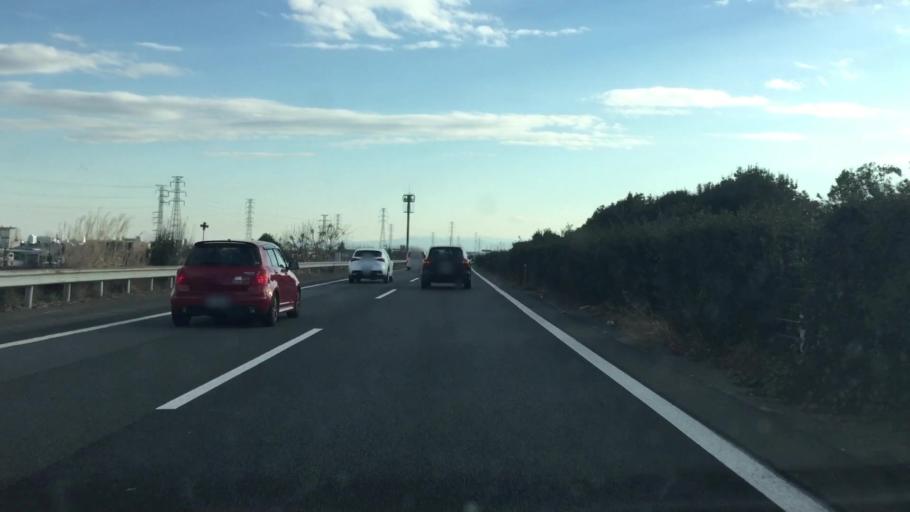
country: JP
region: Gunma
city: Kanekomachi
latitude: 36.4156
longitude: 139.0209
